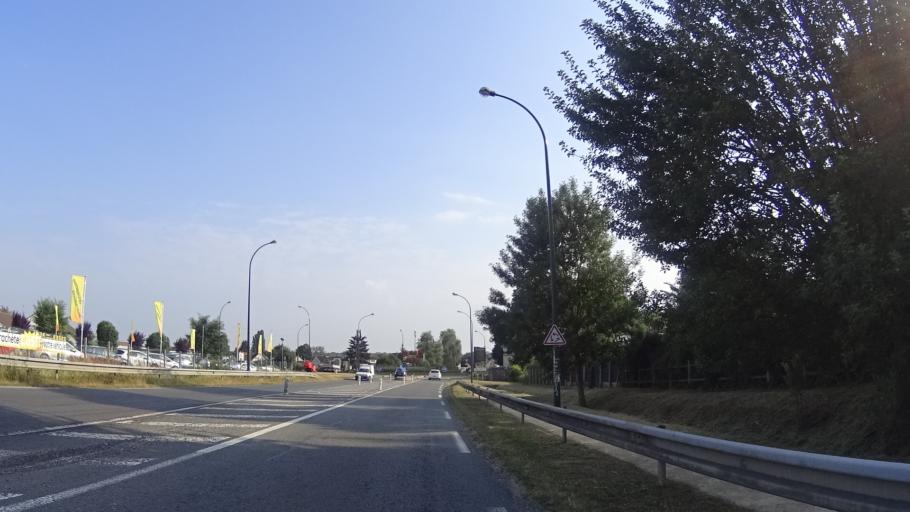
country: FR
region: Ile-de-France
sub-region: Departement du Val-d'Oise
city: Chaumontel
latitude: 49.1221
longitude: 2.4270
